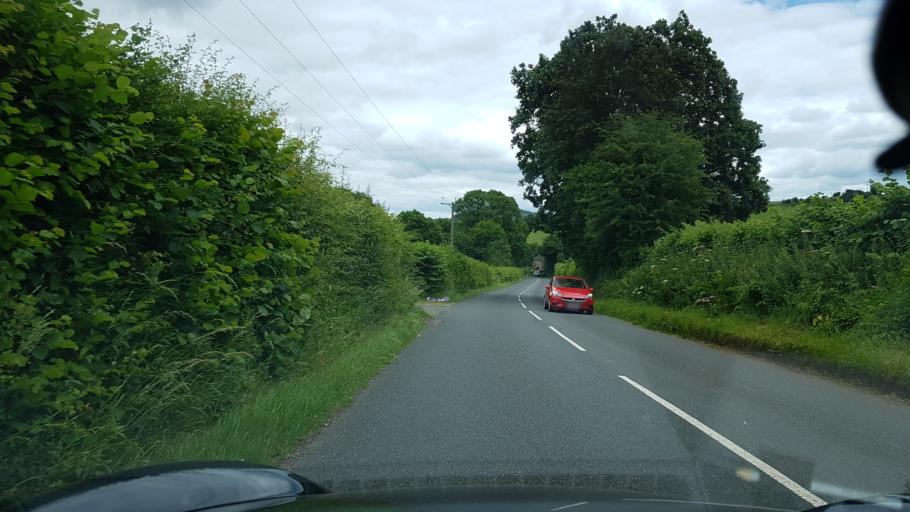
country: GB
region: Wales
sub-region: Monmouthshire
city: Grosmont
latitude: 51.8701
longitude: -2.8331
